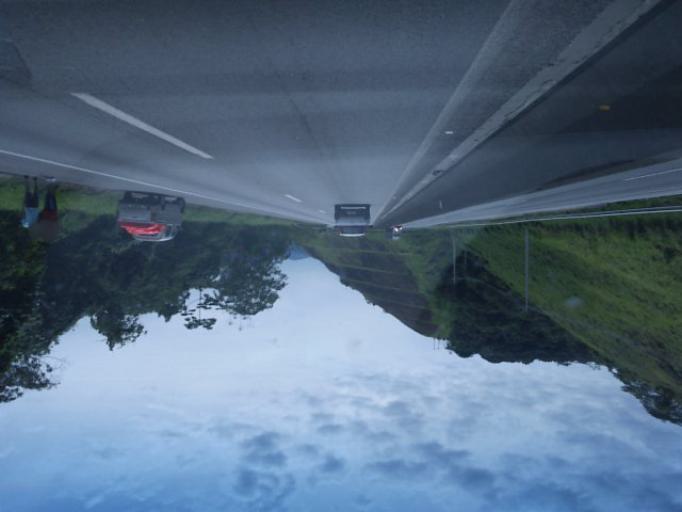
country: BR
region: Sao Paulo
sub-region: Miracatu
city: Miracatu
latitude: -24.1469
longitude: -47.2970
